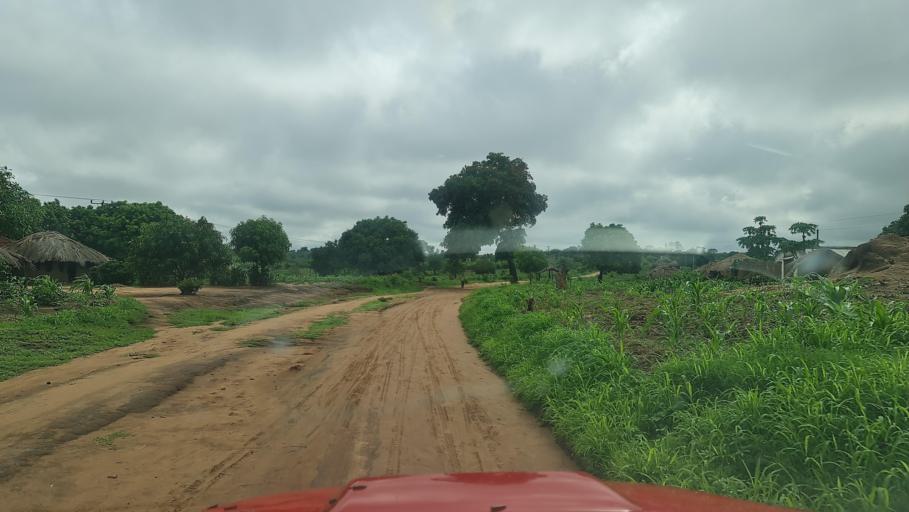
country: MW
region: Southern Region
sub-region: Nsanje District
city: Nsanje
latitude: -17.2030
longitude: 35.6867
